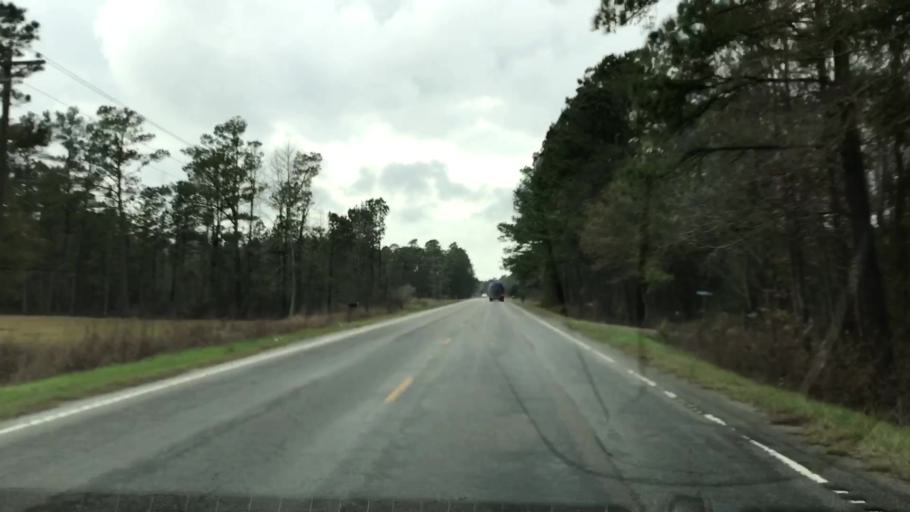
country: US
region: South Carolina
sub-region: Berkeley County
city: Saint Stephen
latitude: 33.2864
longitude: -79.8548
